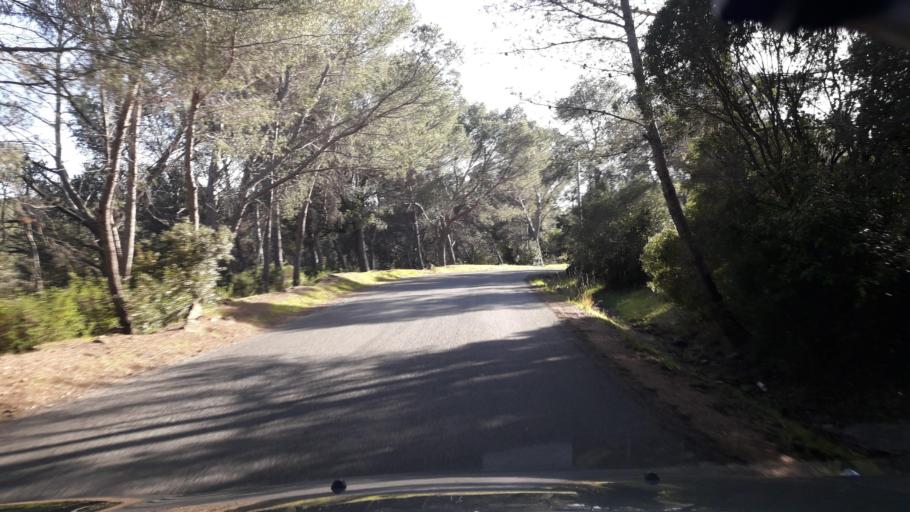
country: FR
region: Provence-Alpes-Cote d'Azur
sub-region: Departement du Var
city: Saint-Raphael
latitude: 43.4204
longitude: 6.8233
